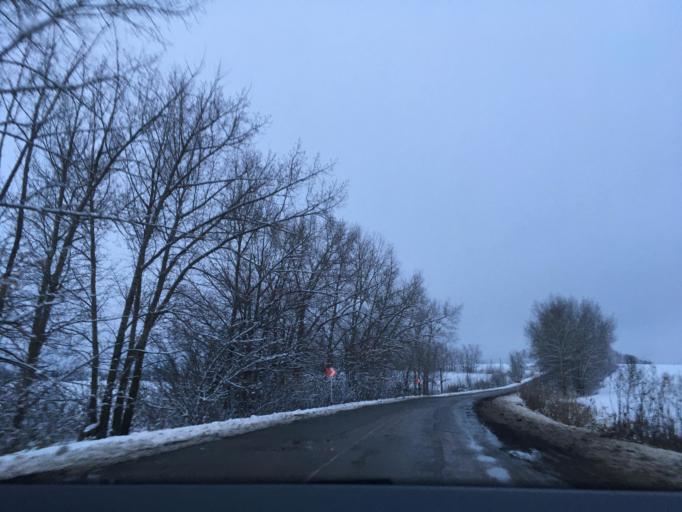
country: RU
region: Voronezj
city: Verkhniy Mamon
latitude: 50.0579
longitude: 40.2561
